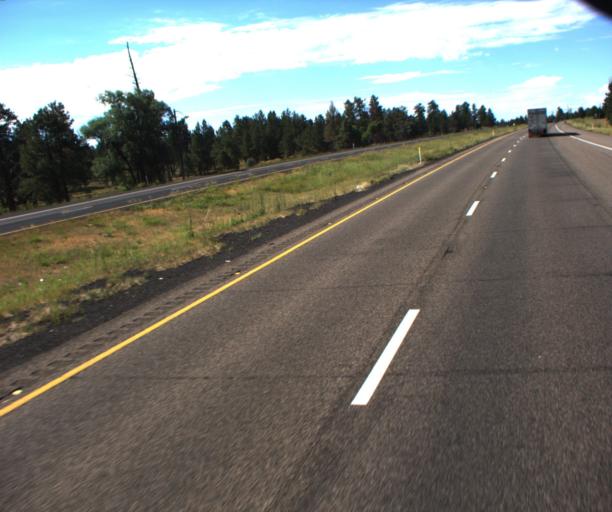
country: US
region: Arizona
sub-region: Coconino County
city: Sedona
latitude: 34.9090
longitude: -111.6414
